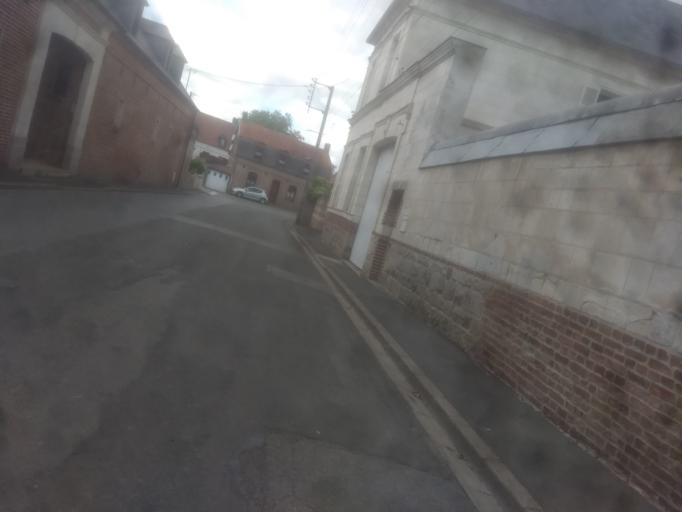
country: FR
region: Nord-Pas-de-Calais
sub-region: Departement du Pas-de-Calais
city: Maroeuil
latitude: 50.3233
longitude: 2.7039
